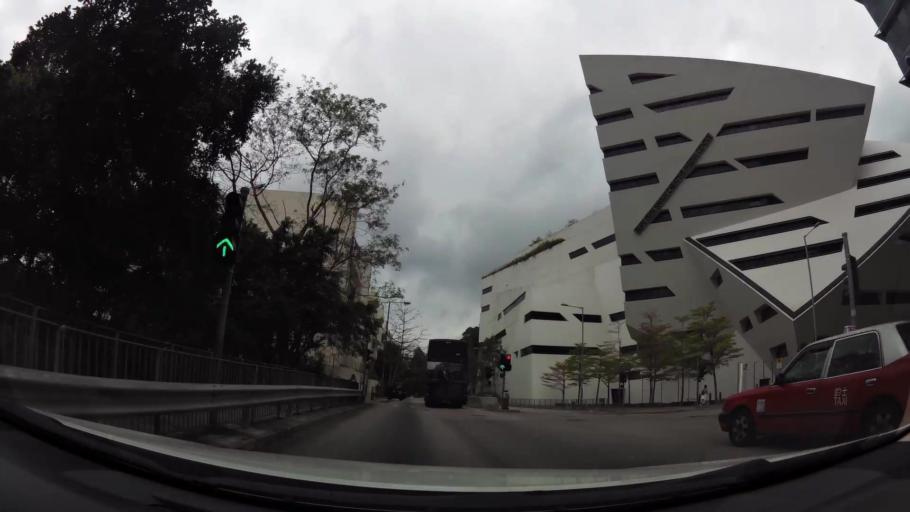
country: HK
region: Sham Shui Po
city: Sham Shui Po
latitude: 22.3396
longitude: 114.1690
